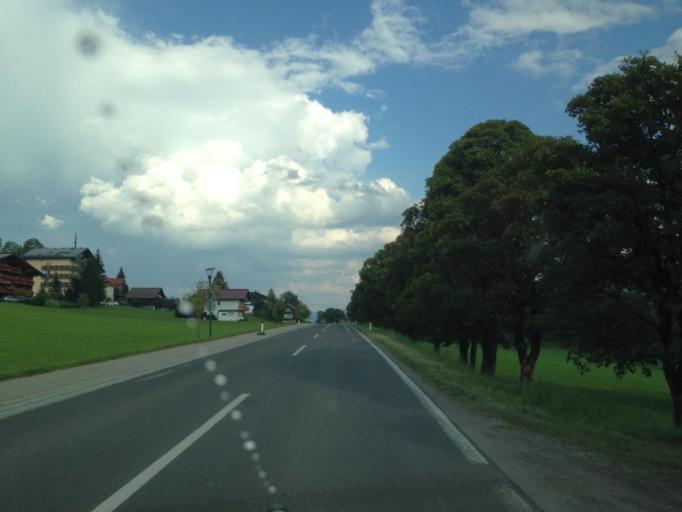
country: AT
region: Styria
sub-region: Politischer Bezirk Liezen
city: Schladming
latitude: 47.4256
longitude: 13.6263
